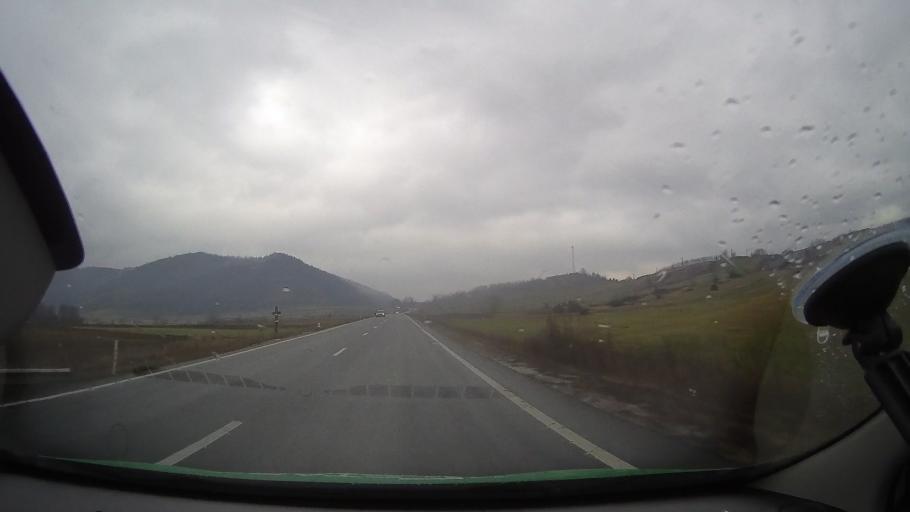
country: RO
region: Hunedoara
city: Vata de Jos
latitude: 46.1858
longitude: 22.6291
